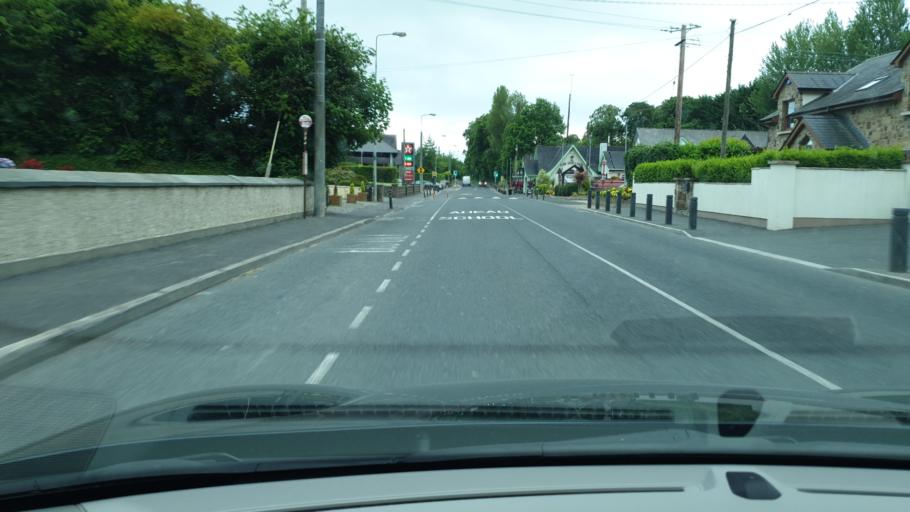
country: IE
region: Leinster
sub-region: An Mhi
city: Dunshaughlin
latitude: 53.4695
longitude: -6.5369
